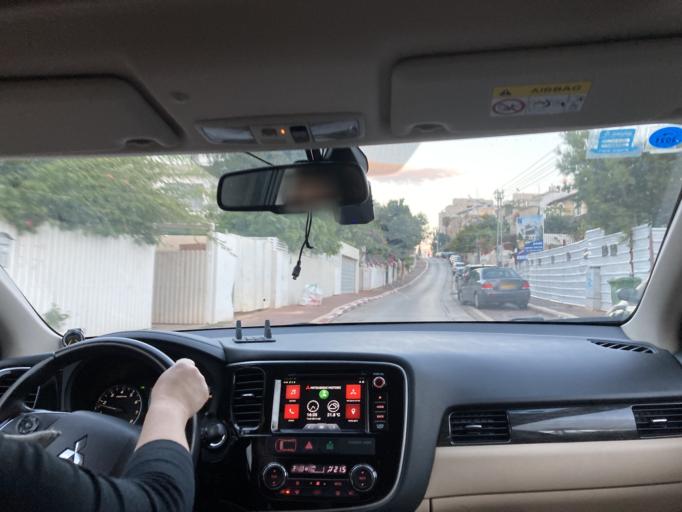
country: IL
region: Tel Aviv
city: Ramat HaSharon
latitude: 32.1499
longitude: 34.8378
